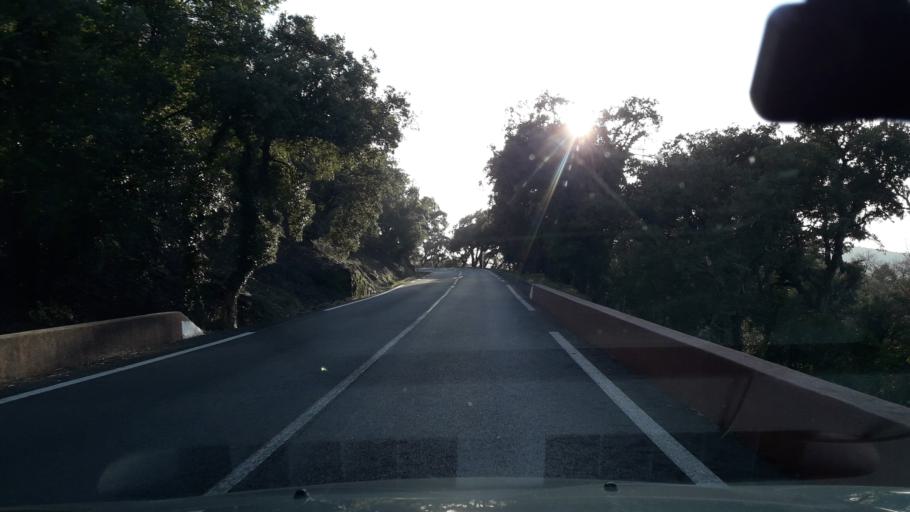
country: FR
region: Provence-Alpes-Cote d'Azur
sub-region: Departement du Var
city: Saint-Raphael
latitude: 43.5116
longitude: 6.8126
